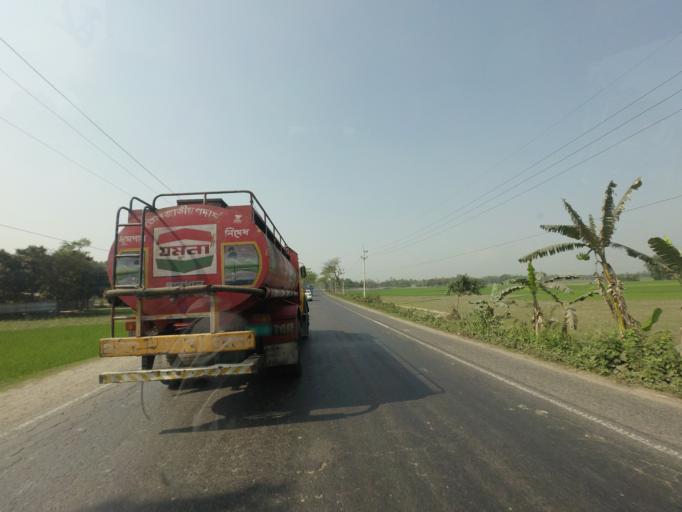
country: BD
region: Sylhet
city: Habiganj
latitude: 24.2930
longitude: 91.5084
